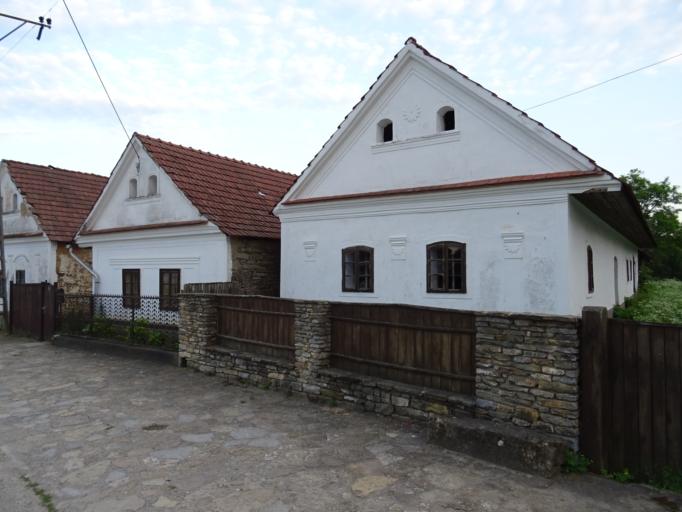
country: HU
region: Borsod-Abauj-Zemplen
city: Szendro
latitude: 48.4724
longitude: 20.6864
